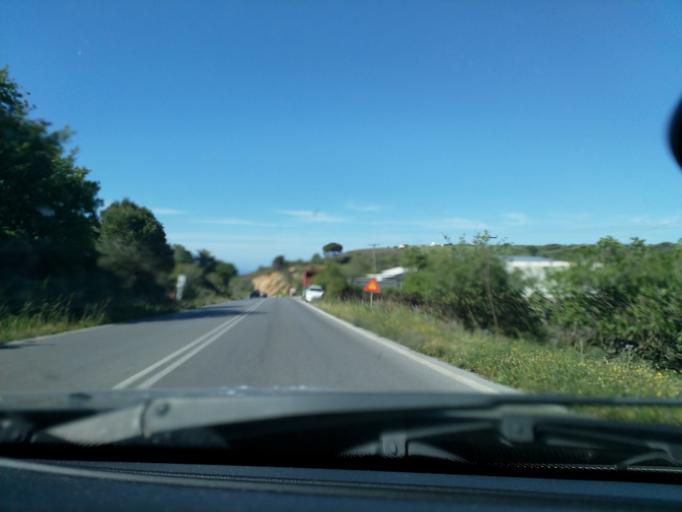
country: GR
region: Crete
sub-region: Nomos Rethymnis
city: Atsipopoulon
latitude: 35.3215
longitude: 24.4646
